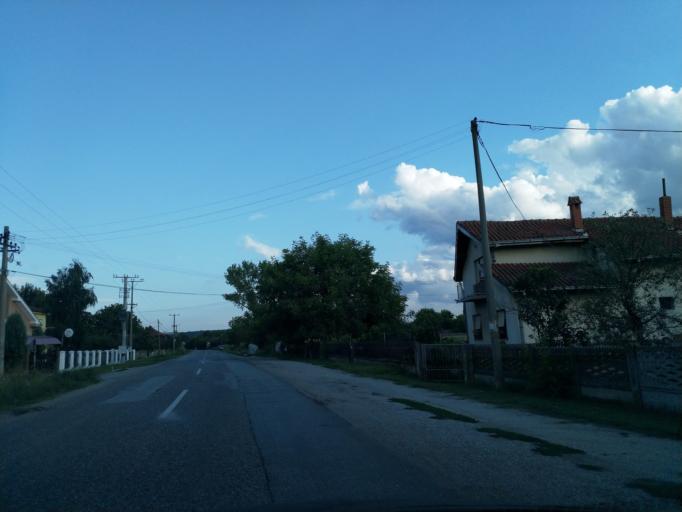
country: RS
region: Central Serbia
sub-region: Rasinski Okrug
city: Cicevac
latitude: 43.7566
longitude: 21.4345
